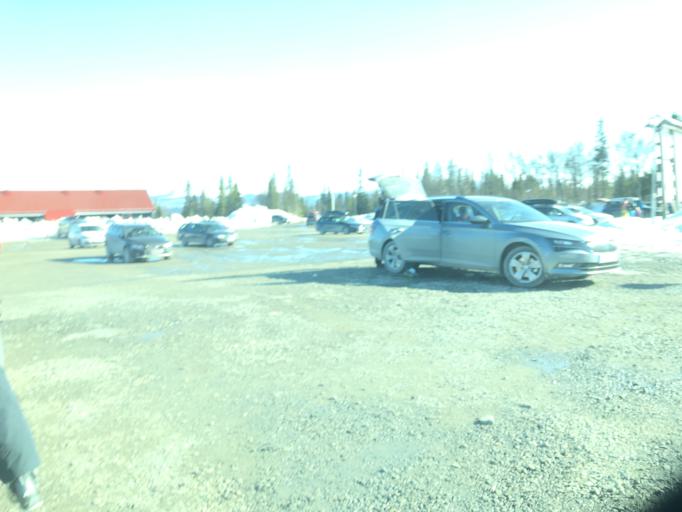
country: SE
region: Jaemtland
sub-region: Are Kommun
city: Are
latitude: 63.2665
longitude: 13.1612
